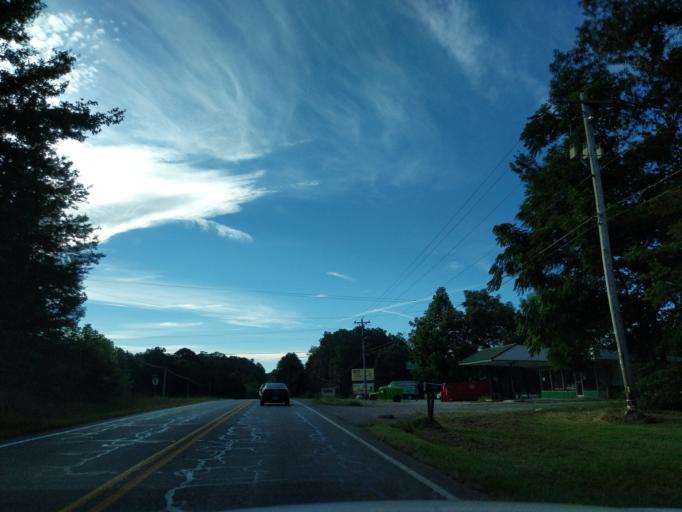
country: US
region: Georgia
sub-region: Fannin County
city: Blue Ridge
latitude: 34.8922
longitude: -84.3506
